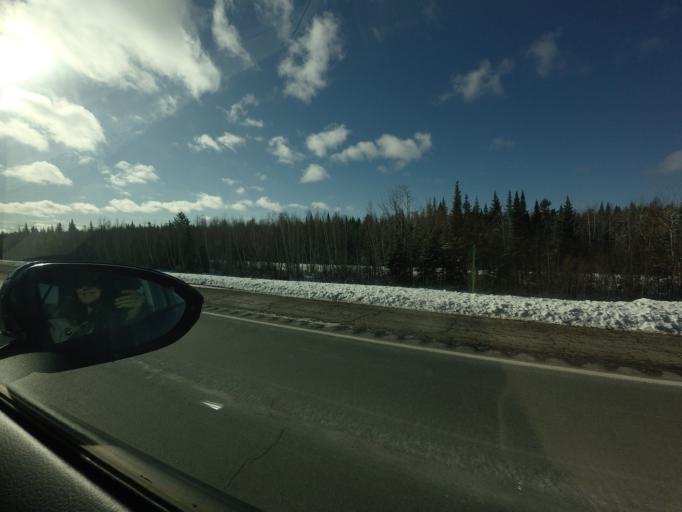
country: CA
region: New Brunswick
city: Fredericton
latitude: 45.8817
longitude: -66.6377
